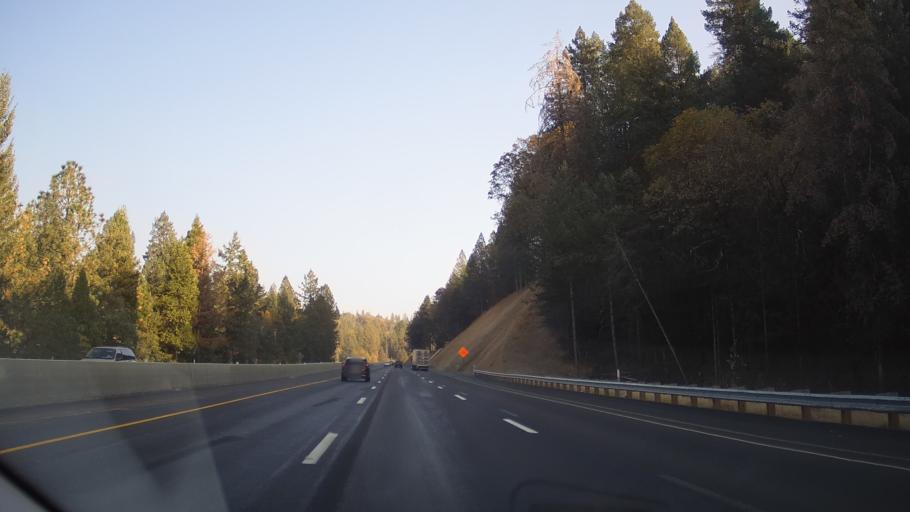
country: US
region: California
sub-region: Placer County
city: Colfax
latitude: 39.1389
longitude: -120.9247
